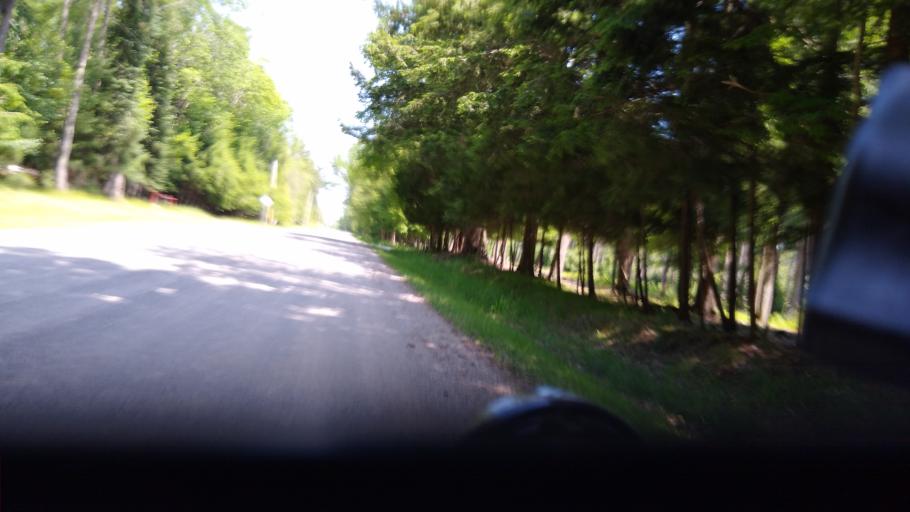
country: US
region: Michigan
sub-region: Delta County
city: Escanaba
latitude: 45.7101
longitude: -87.1573
